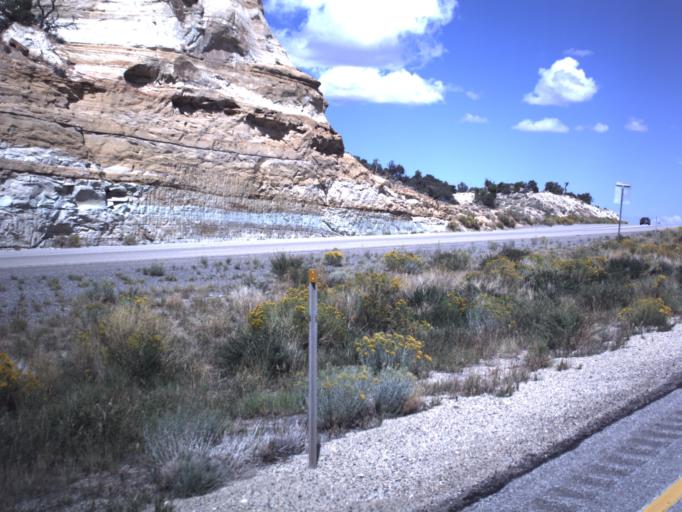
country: US
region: Utah
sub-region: Emery County
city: Ferron
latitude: 38.8601
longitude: -110.8172
